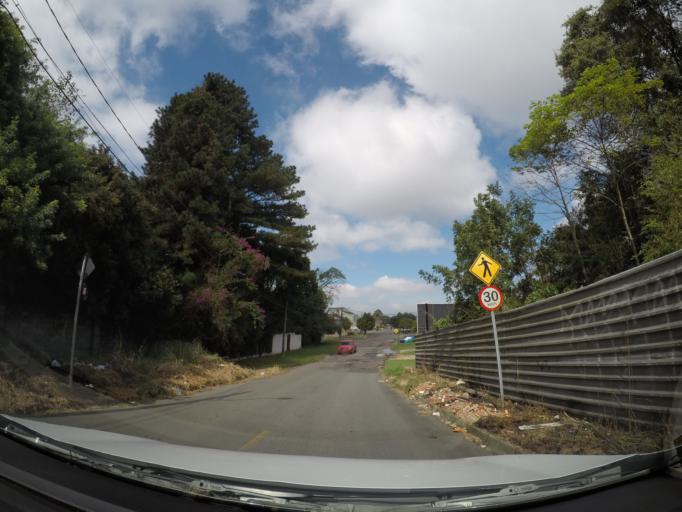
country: BR
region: Parana
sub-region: Sao Jose Dos Pinhais
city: Sao Jose dos Pinhais
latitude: -25.4893
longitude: -49.2200
